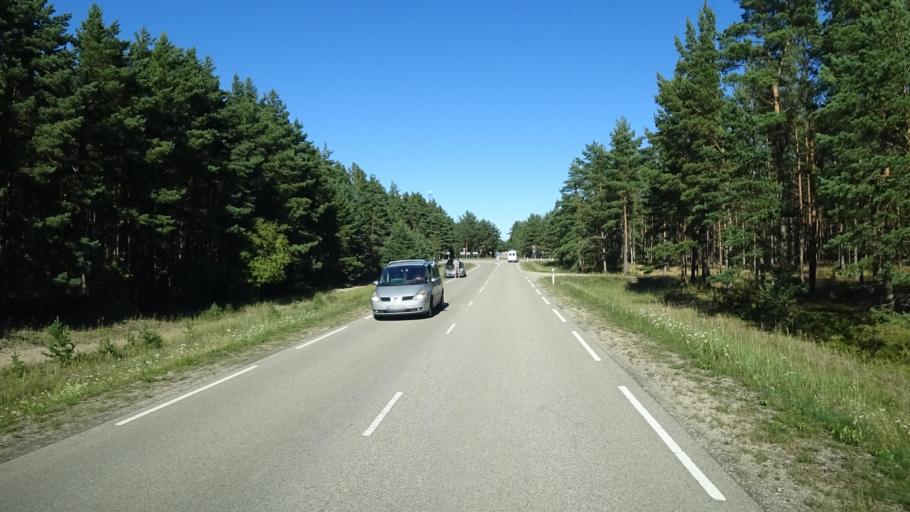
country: LV
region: Dundaga
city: Dundaga
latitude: 57.7543
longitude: 22.5917
